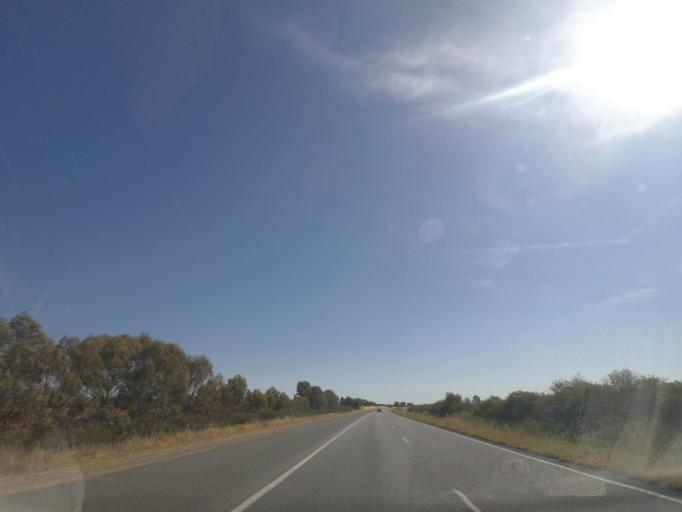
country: AU
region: Victoria
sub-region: Greater Shepparton
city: Shepparton
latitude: -36.6650
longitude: 145.2747
